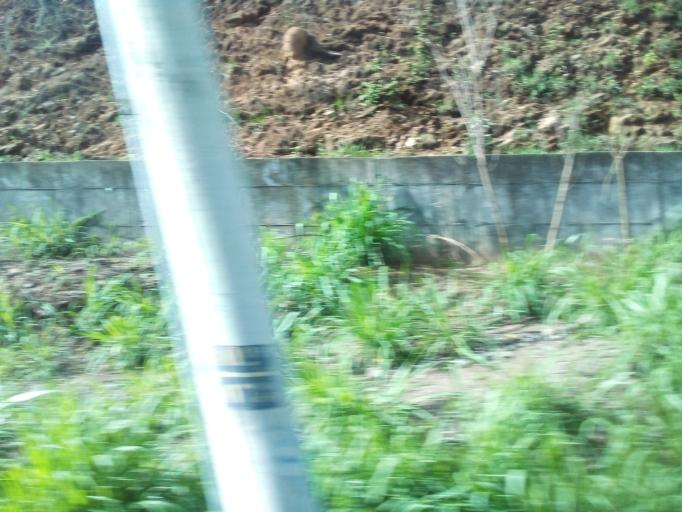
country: BR
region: Minas Gerais
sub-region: Raposos
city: Raposos
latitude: -19.8699
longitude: -43.8282
